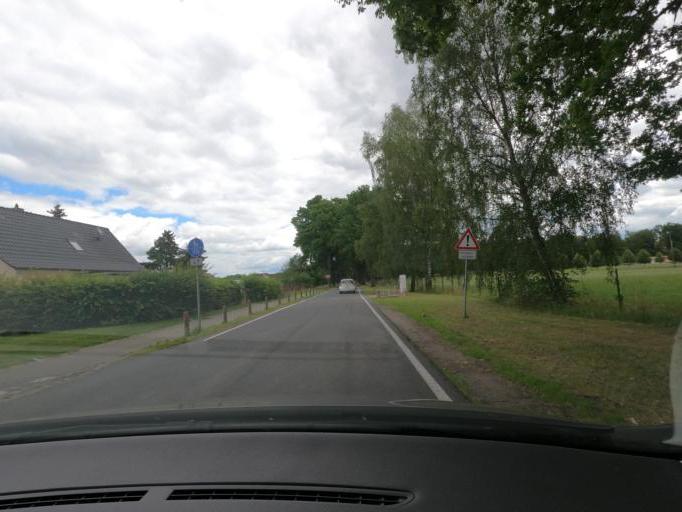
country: DE
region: Brandenburg
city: Kremmen
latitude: 52.7287
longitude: 12.9608
